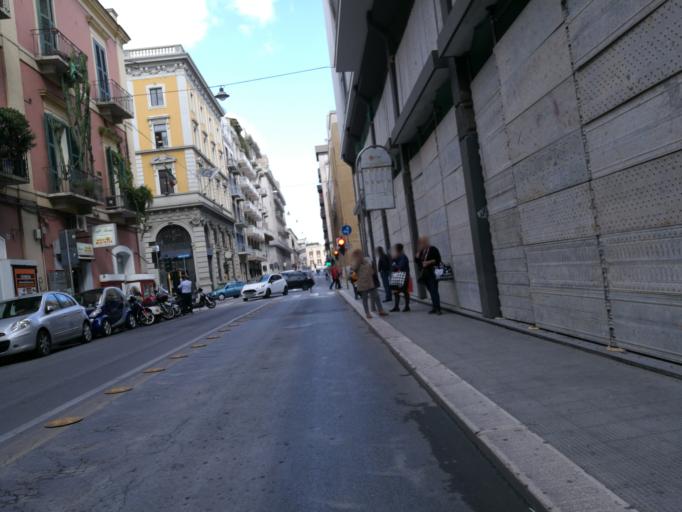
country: IT
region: Apulia
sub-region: Provincia di Bari
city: Bari
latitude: 41.1235
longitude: 16.8690
